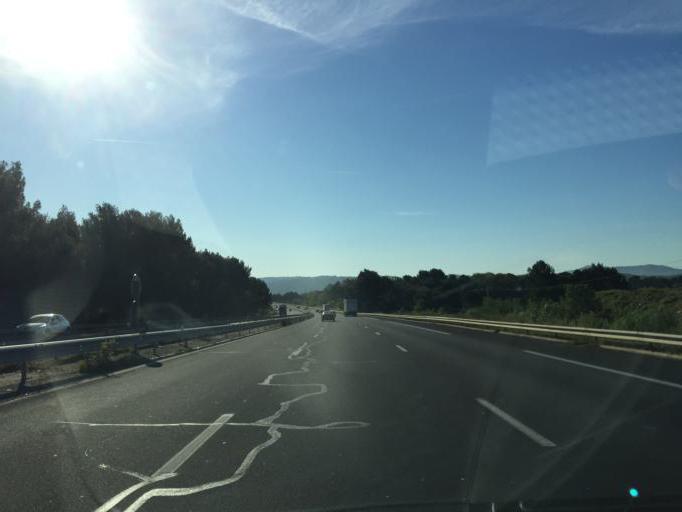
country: FR
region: Provence-Alpes-Cote d'Azur
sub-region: Departement des Bouches-du-Rhone
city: Aix-en-Provence
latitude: 43.5235
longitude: 5.4084
